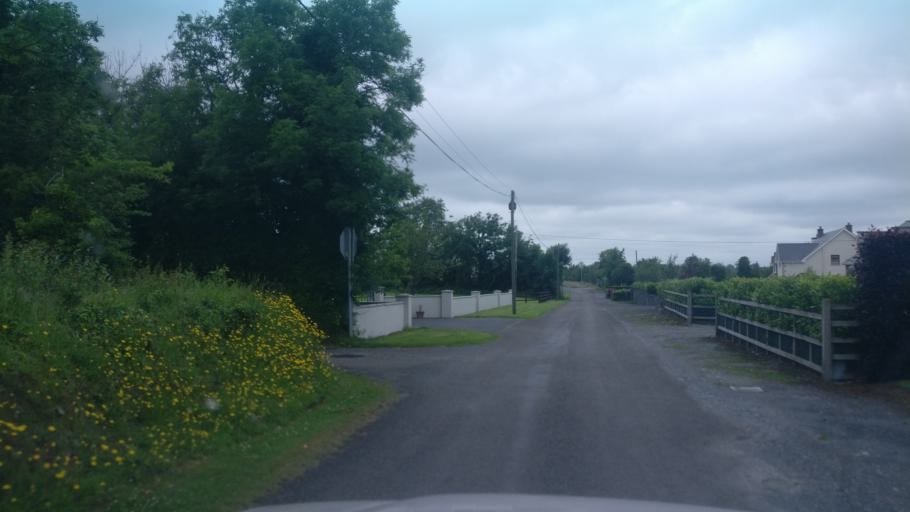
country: IE
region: Connaught
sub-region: County Galway
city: Ballinasloe
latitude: 53.2962
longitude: -8.3416
